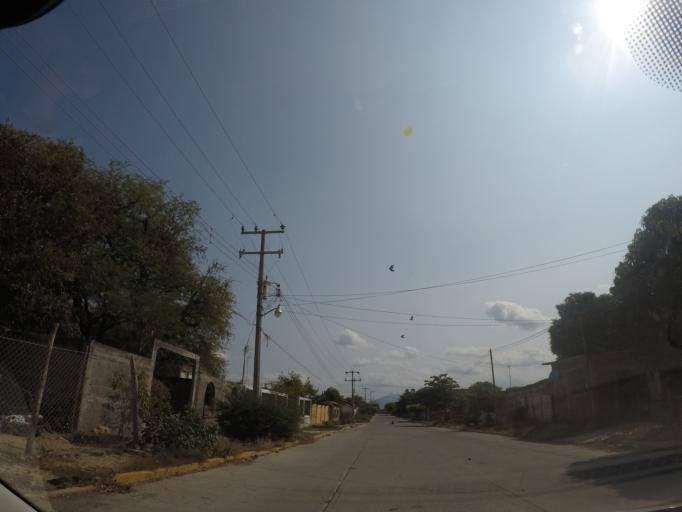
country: MX
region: Oaxaca
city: San Jeronimo Ixtepec
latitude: 16.5474
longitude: -95.0885
